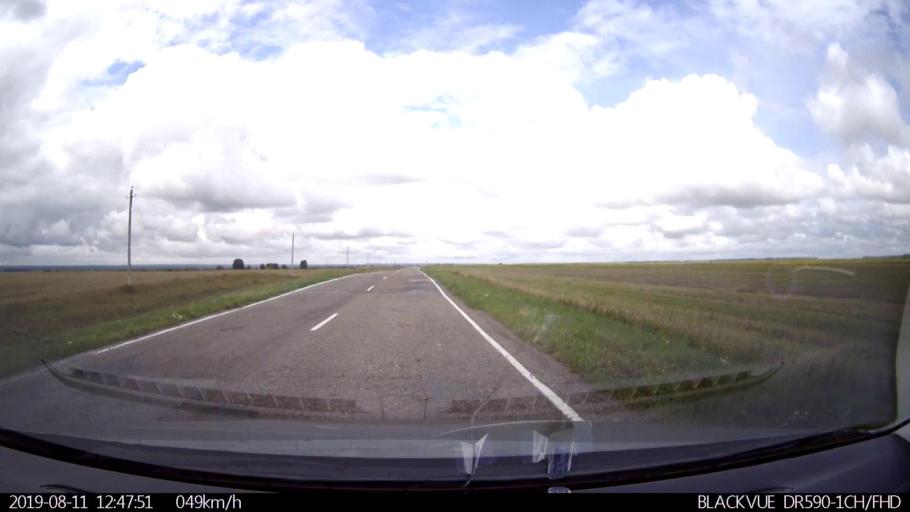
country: RU
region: Ulyanovsk
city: Ignatovka
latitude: 53.8713
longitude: 47.7047
